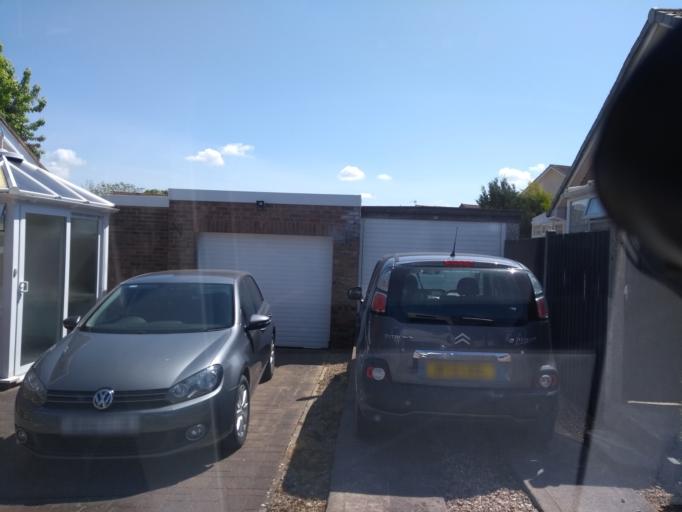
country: GB
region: England
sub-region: Somerset
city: North Petherton
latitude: 51.0900
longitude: -3.0130
